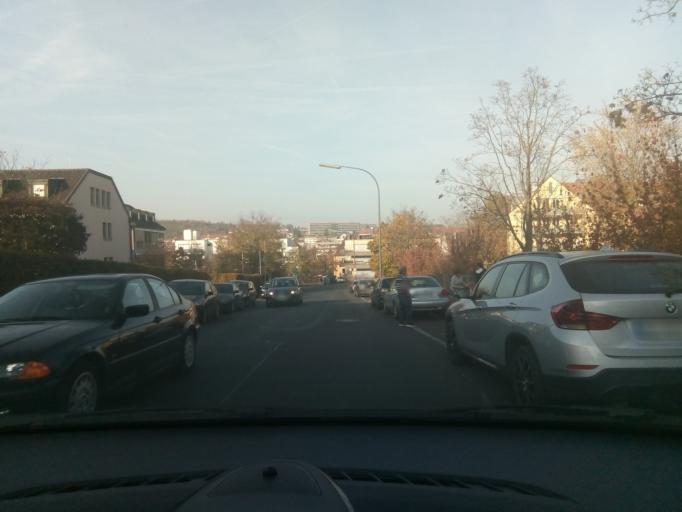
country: DE
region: Bavaria
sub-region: Regierungsbezirk Unterfranken
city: Wuerzburg
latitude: 49.7954
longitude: 9.9529
